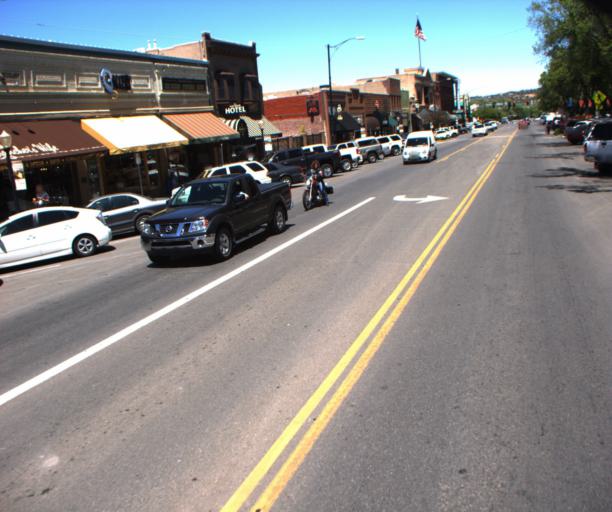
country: US
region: Arizona
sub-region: Yavapai County
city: Prescott
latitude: 34.5402
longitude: -112.4701
